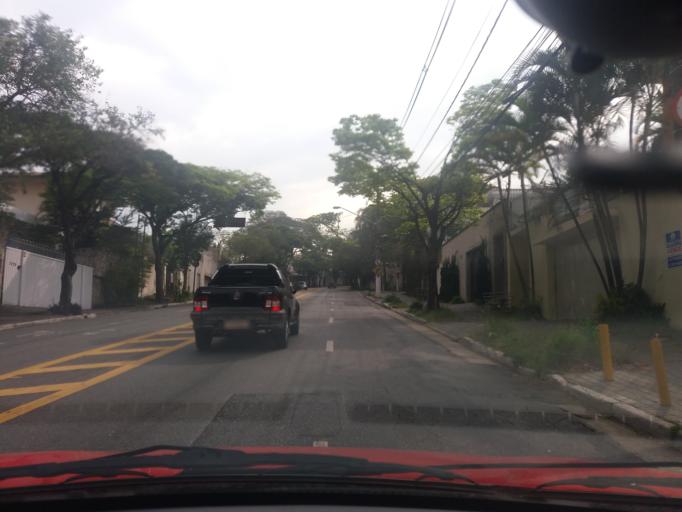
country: BR
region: Sao Paulo
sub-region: Taboao Da Serra
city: Taboao da Serra
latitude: -23.5964
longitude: -46.7188
